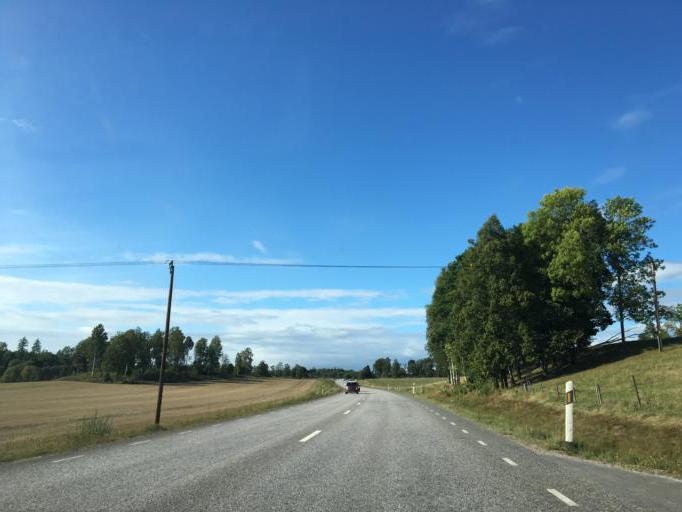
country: SE
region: Soedermanland
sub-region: Nykopings Kommun
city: Nykoping
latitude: 58.8146
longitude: 16.9428
